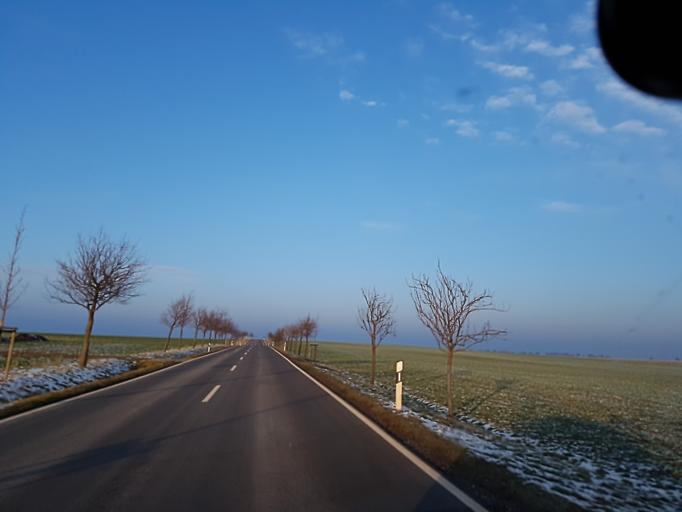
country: DE
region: Saxony
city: Strehla
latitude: 51.3211
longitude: 13.1965
